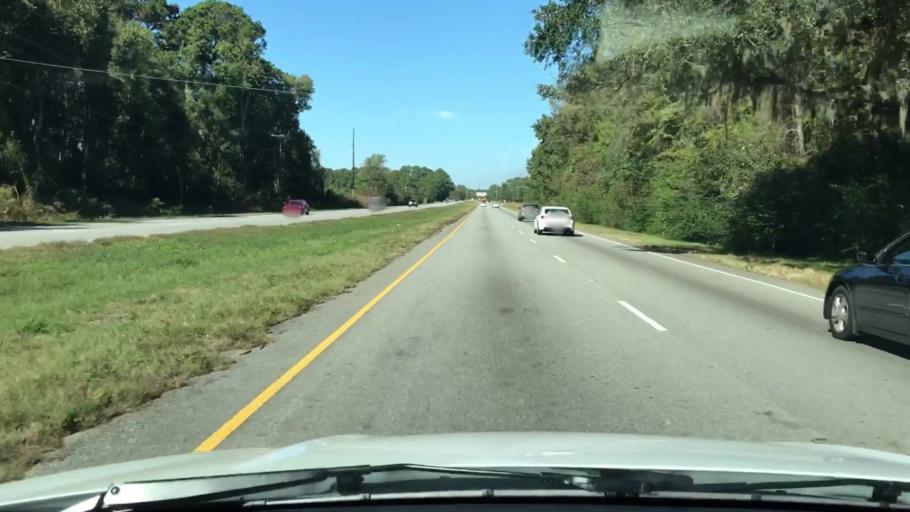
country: US
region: South Carolina
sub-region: Beaufort County
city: Laurel Bay
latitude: 32.4986
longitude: -80.7434
